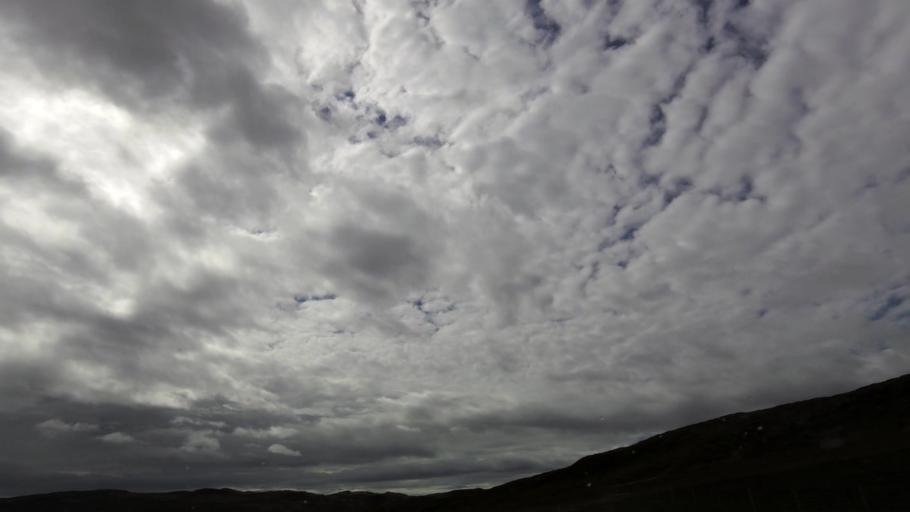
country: IS
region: West
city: Stykkisholmur
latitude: 65.5378
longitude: -22.0667
